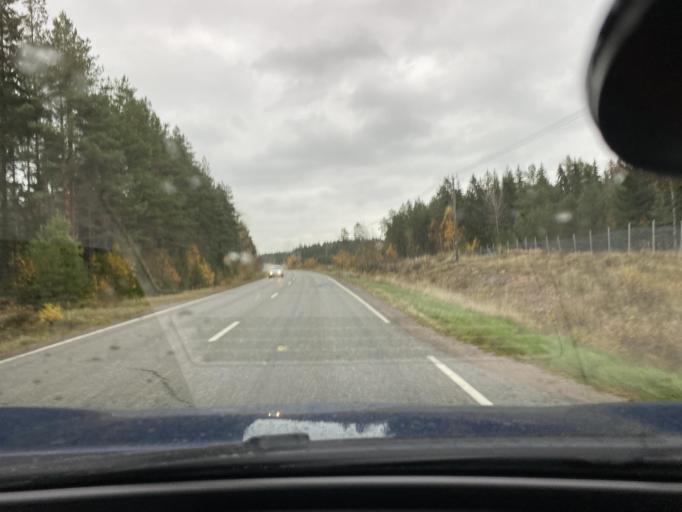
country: FI
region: Satakunta
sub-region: Rauma
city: Saekylae
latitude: 61.0481
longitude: 22.4295
